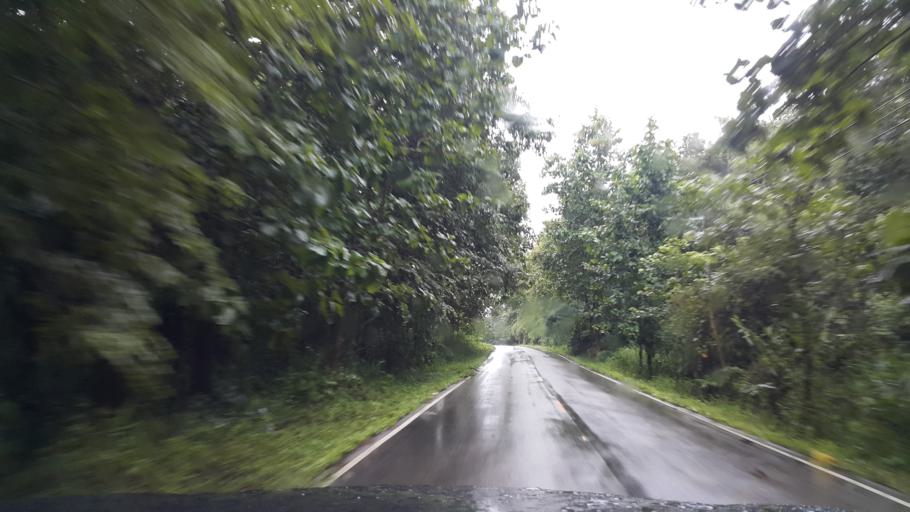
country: TH
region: Phayao
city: Phu Sang
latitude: 19.6087
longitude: 100.4077
